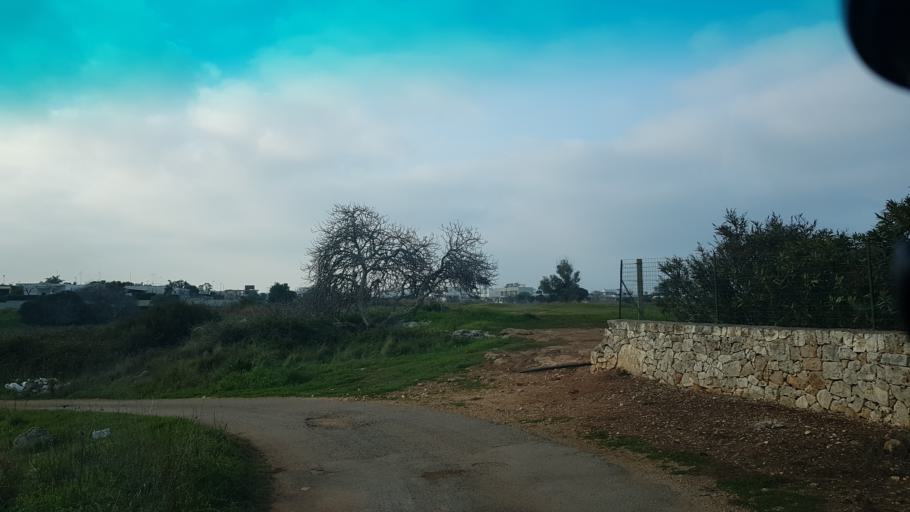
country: IT
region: Apulia
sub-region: Provincia di Brindisi
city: Carovigno
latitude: 40.7439
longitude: 17.7213
